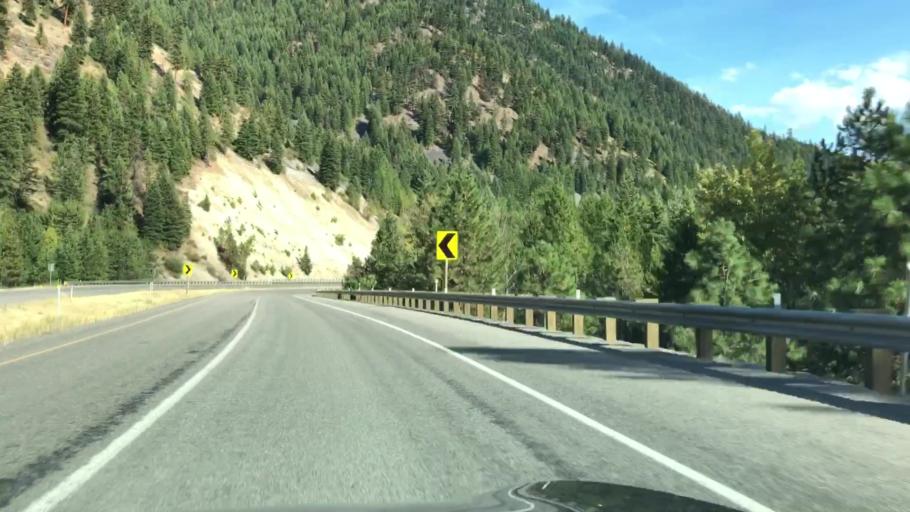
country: US
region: Montana
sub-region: Sanders County
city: Thompson Falls
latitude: 47.3273
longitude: -115.2546
